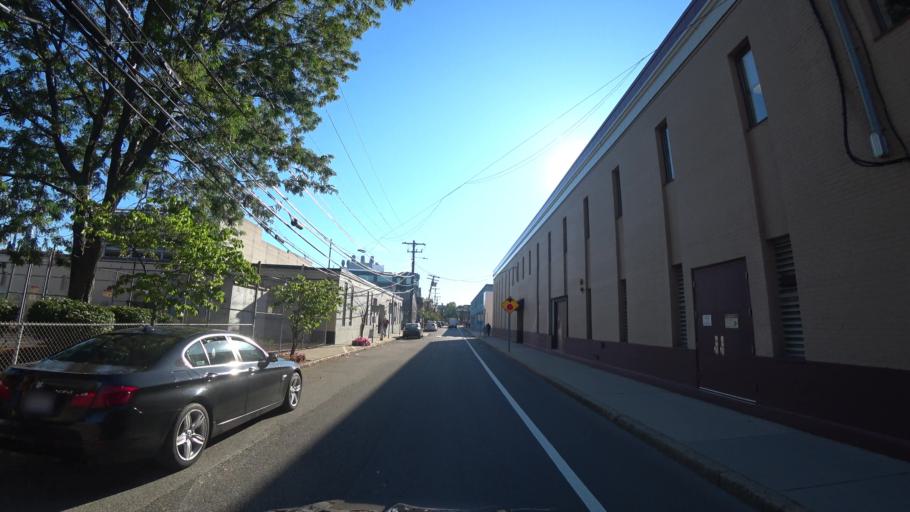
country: US
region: Massachusetts
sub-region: Middlesex County
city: Cambridge
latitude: 42.3593
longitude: -71.1038
